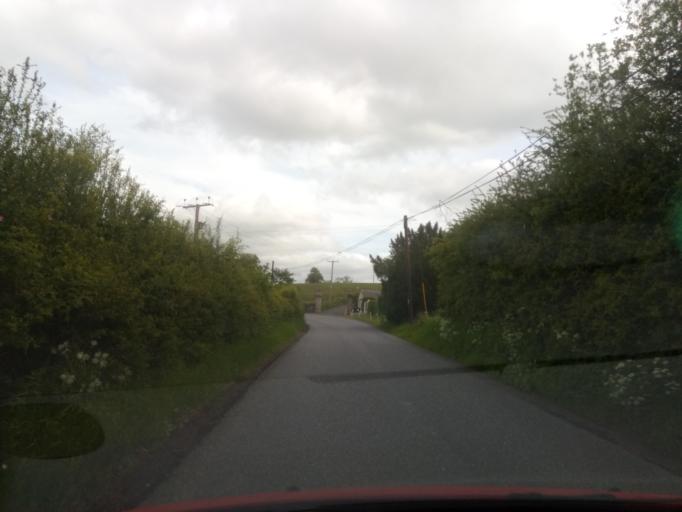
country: GB
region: Scotland
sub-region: The Scottish Borders
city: Selkirk
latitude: 55.5422
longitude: -2.8545
